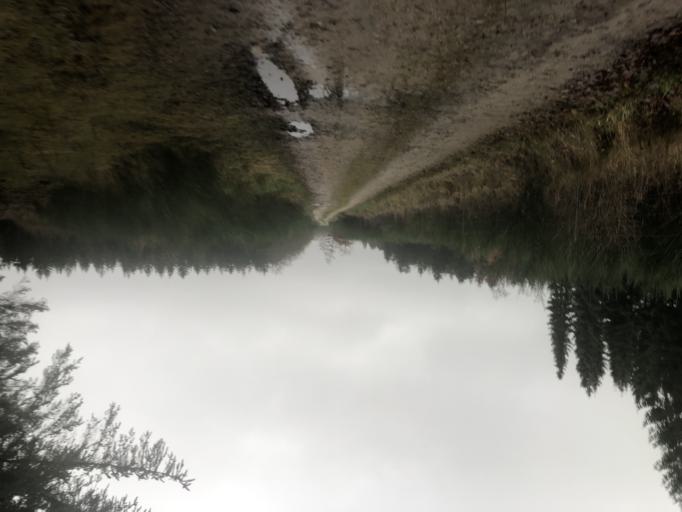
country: DK
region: Central Jutland
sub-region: Holstebro Kommune
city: Ulfborg
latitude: 56.2955
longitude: 8.4409
